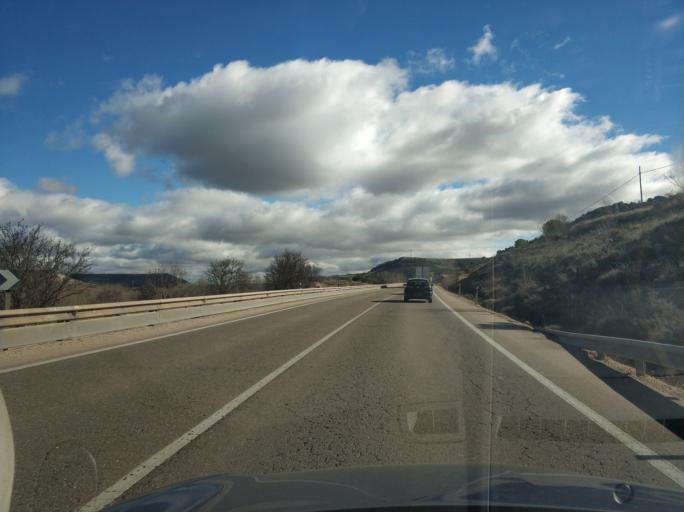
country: ES
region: Castille and Leon
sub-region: Provincia de Valladolid
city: Bocos de Duero
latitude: 41.6114
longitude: -4.0887
